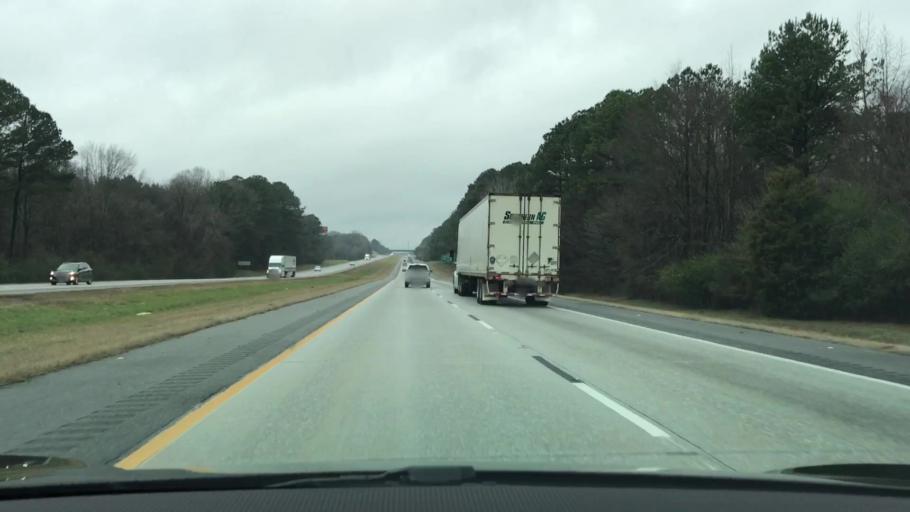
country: US
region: Georgia
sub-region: Putnam County
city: Jefferson
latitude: 33.5467
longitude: -83.3397
